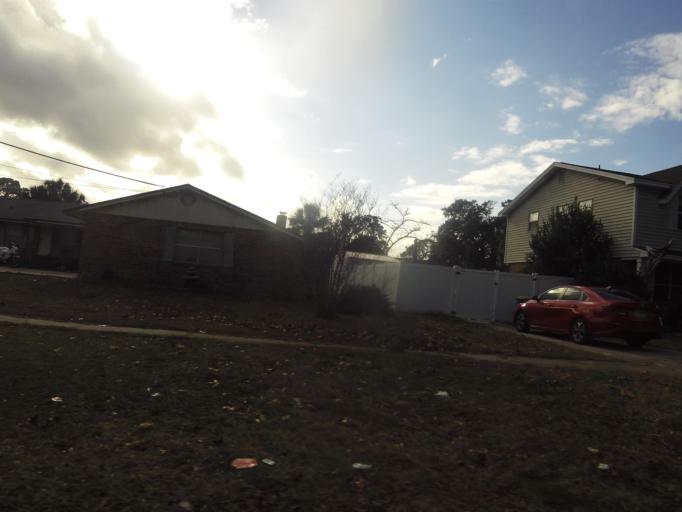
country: US
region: Florida
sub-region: Duval County
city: Jacksonville
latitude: 30.3416
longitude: -81.5773
